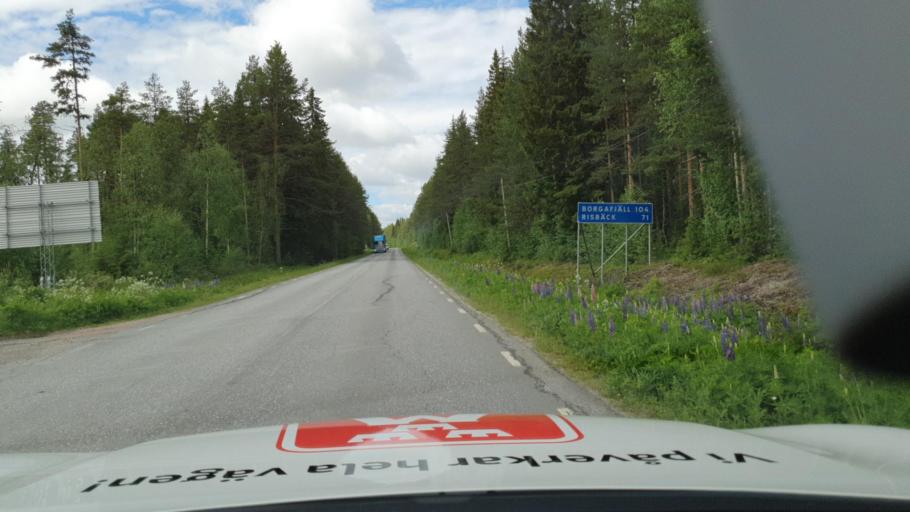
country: SE
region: Vaesterbotten
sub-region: Dorotea Kommun
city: Dorotea
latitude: 64.2604
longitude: 16.3739
